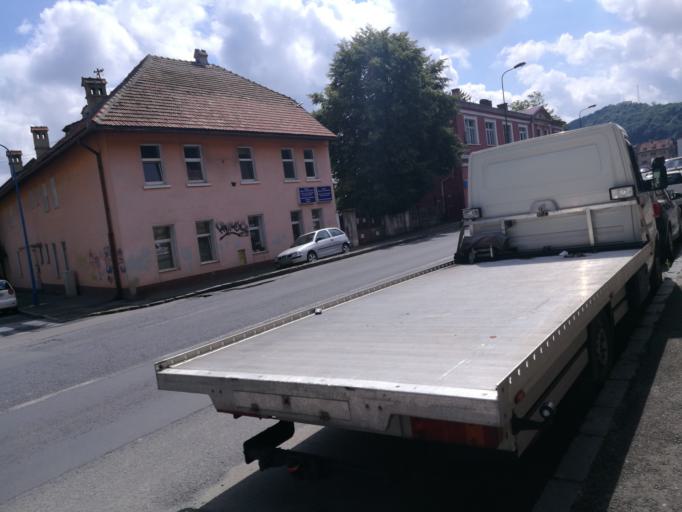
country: RO
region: Brasov
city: Brasov
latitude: 45.6507
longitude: 25.5964
